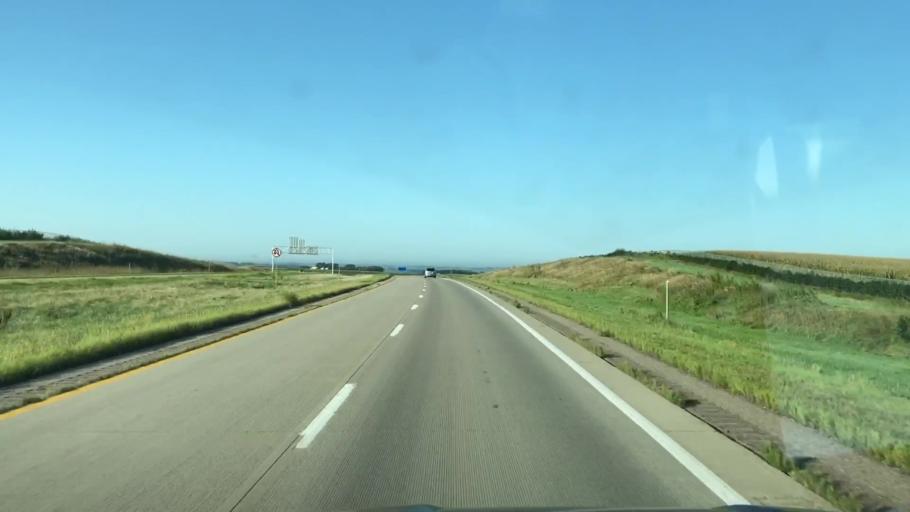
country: US
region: Iowa
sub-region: Plymouth County
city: Le Mars
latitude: 42.8112
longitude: -96.1953
